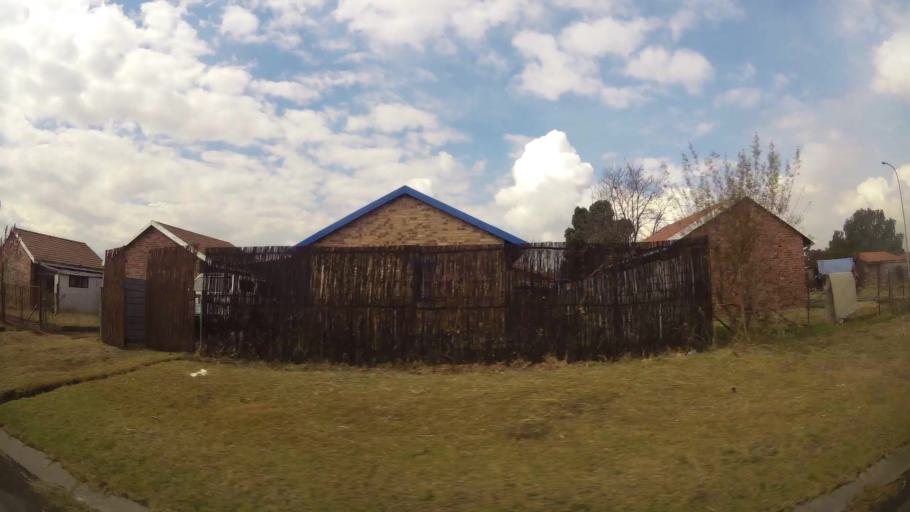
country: ZA
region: Gauteng
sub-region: Sedibeng District Municipality
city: Vereeniging
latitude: -26.6634
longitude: 27.9135
